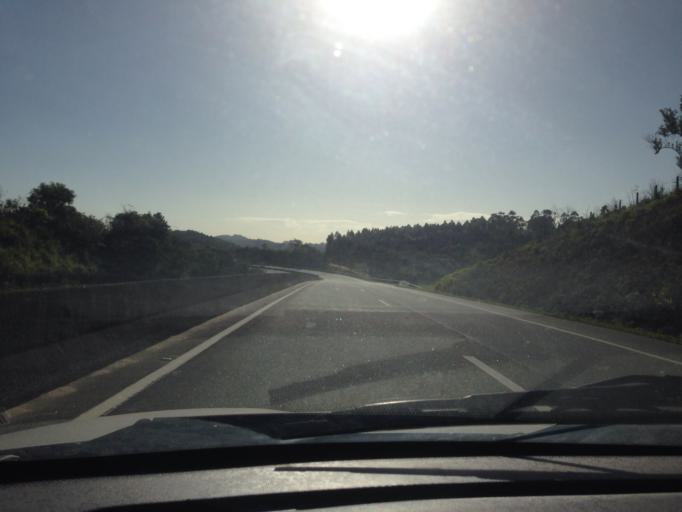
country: BR
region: Espirito Santo
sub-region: Guarapari
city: Guarapari
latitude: -20.6254
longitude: -40.4982
